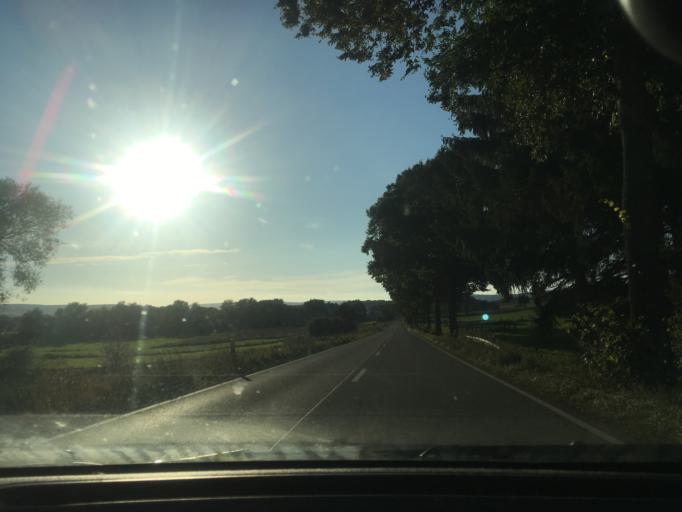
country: DE
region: Lower Saxony
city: Eimen
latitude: 51.8204
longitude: 9.8004
